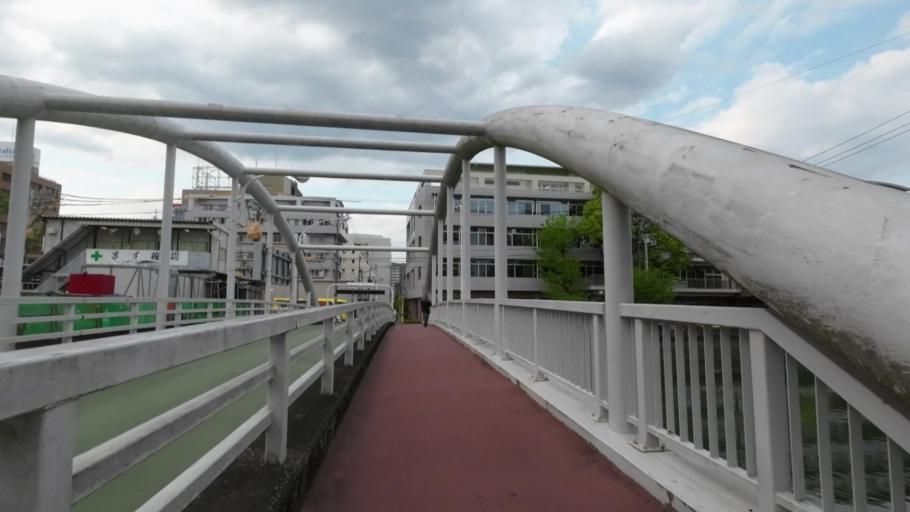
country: JP
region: Kochi
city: Kochi-shi
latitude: 33.5637
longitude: 133.5441
